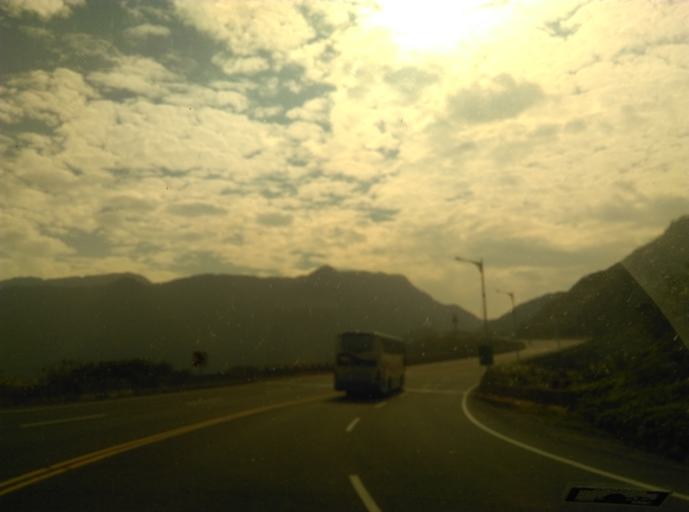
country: TW
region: Taiwan
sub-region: Keelung
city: Keelung
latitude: 25.1701
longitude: 121.7082
